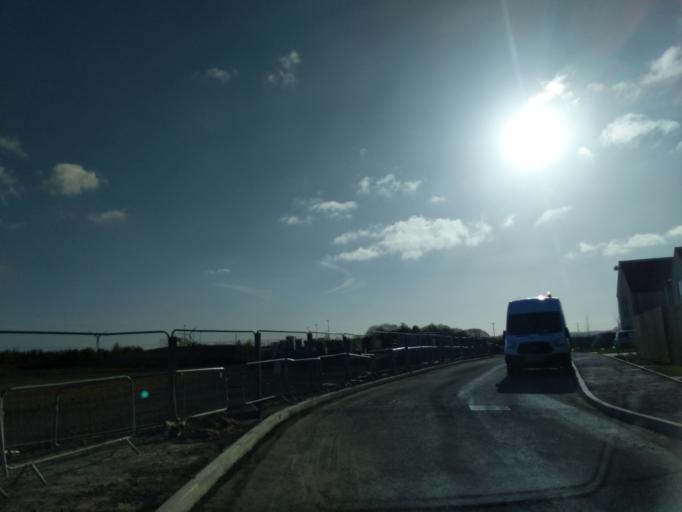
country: GB
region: England
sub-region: Northumberland
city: Cresswell
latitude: 55.2190
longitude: -1.5586
